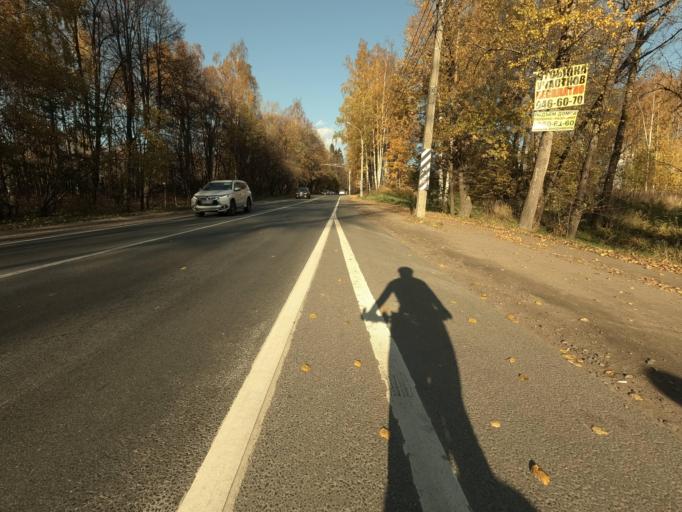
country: RU
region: St.-Petersburg
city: Pargolovo
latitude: 60.1075
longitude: 30.2486
